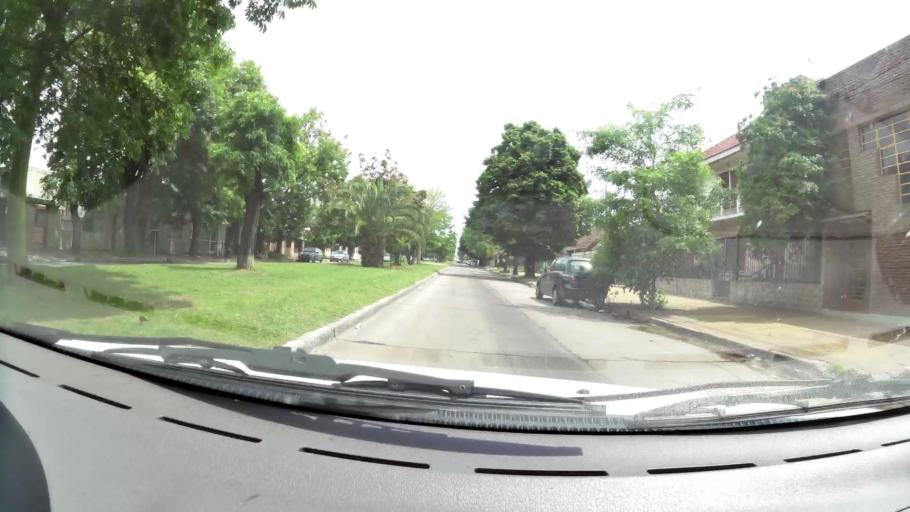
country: AR
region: Buenos Aires
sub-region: Partido de La Plata
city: La Plata
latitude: -34.9461
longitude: -57.9569
